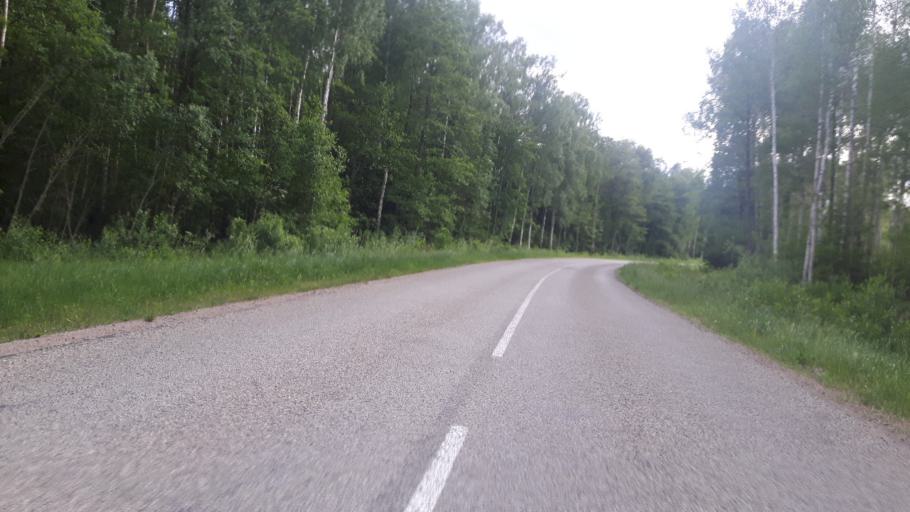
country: LV
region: Engure
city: Smarde
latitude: 57.0272
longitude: 23.3576
